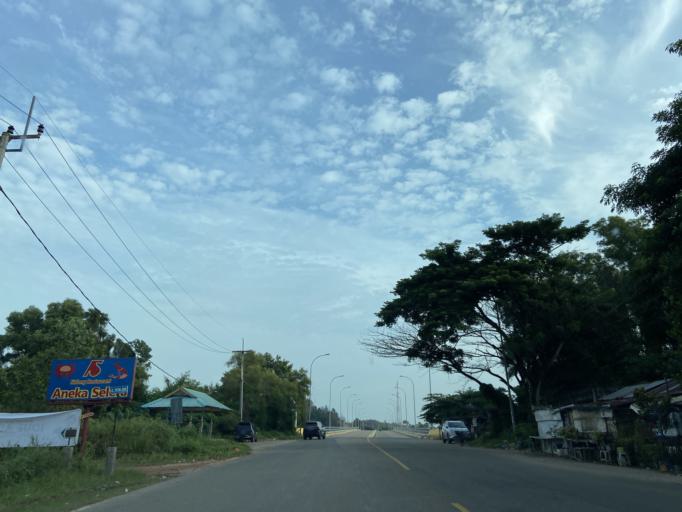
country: ID
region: Riau Islands
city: Tanjungpinang
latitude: 0.9440
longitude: 104.0792
